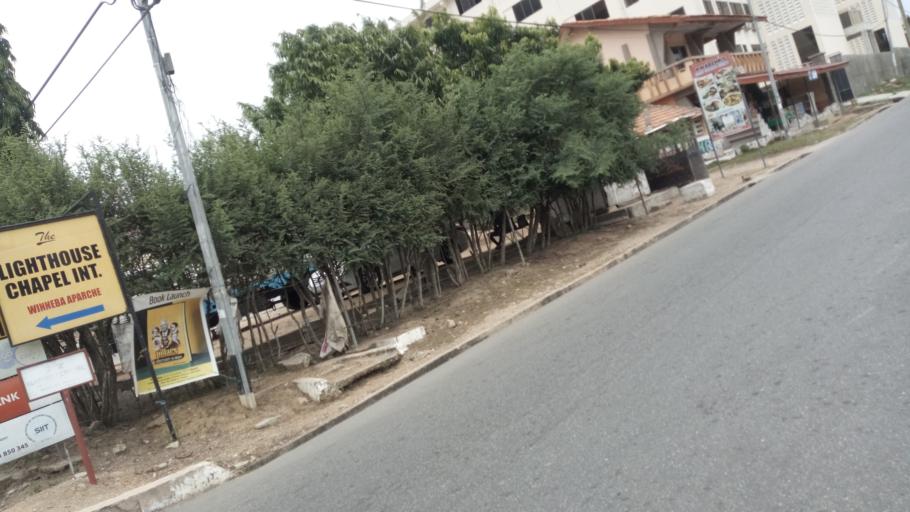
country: GH
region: Central
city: Winneba
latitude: 5.3455
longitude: -0.6267
